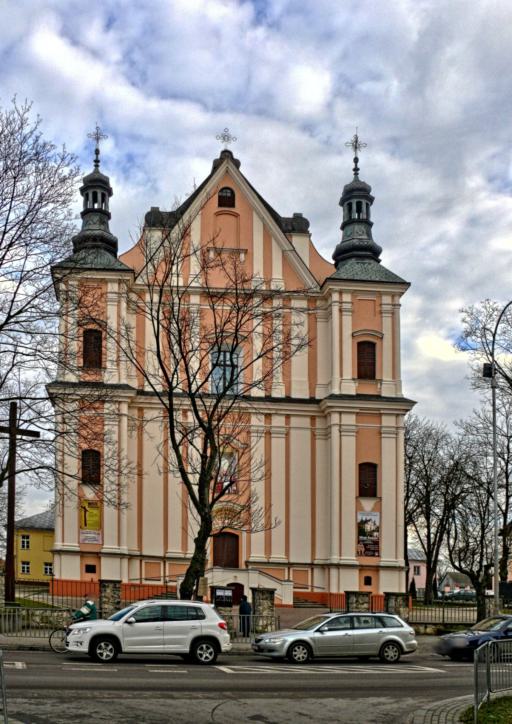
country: PL
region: Lublin Voivodeship
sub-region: Powiat lukowski
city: Lukow
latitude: 51.9243
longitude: 22.3868
